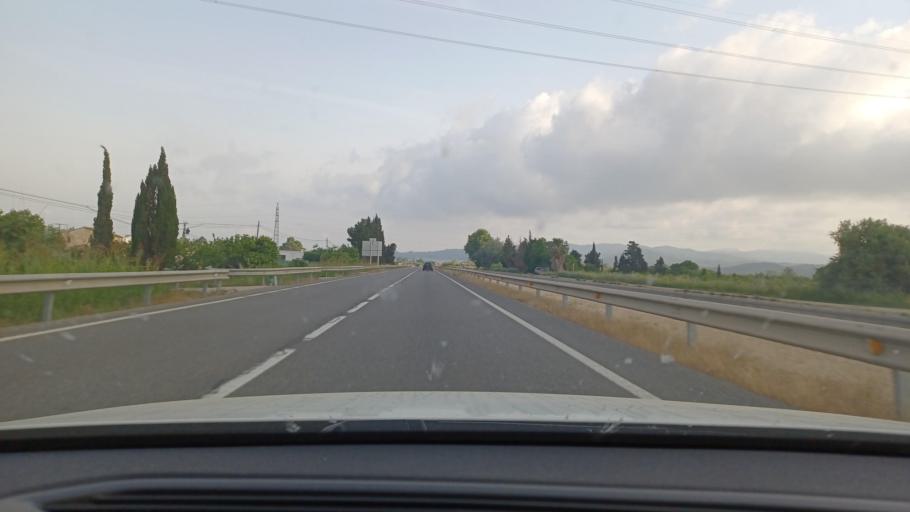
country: ES
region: Catalonia
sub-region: Provincia de Tarragona
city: Amposta
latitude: 40.7302
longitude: 0.5703
